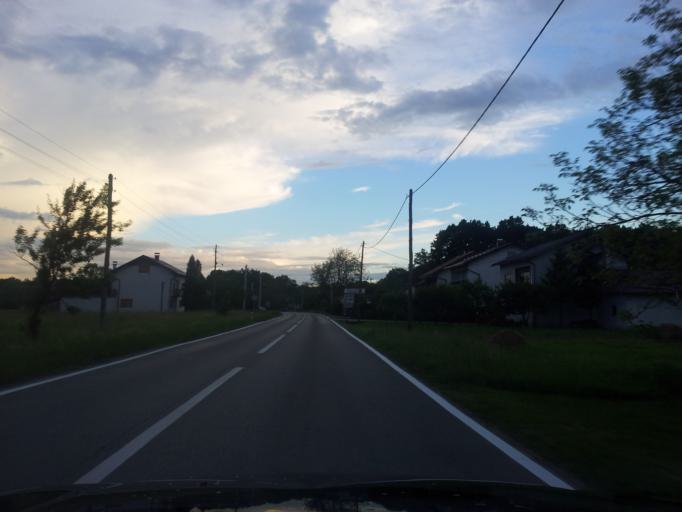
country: HR
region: Karlovacka
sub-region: Grad Karlovac
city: Karlovac
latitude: 45.5479
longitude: 15.5707
